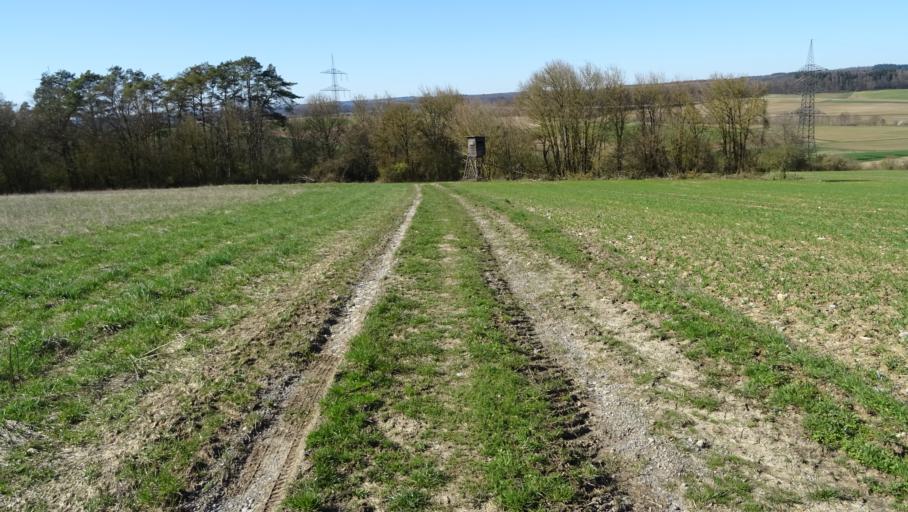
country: DE
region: Baden-Wuerttemberg
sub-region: Karlsruhe Region
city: Seckach
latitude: 49.4288
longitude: 9.3119
